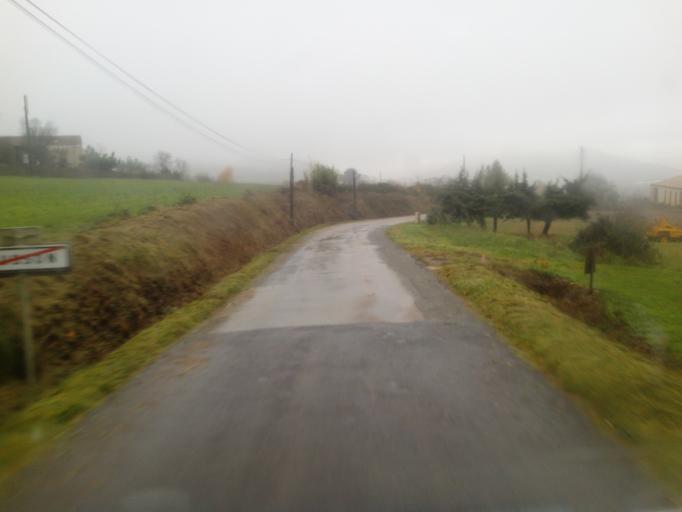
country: FR
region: Languedoc-Roussillon
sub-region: Departement de l'Herault
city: Nebian
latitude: 43.6360
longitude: 3.3677
